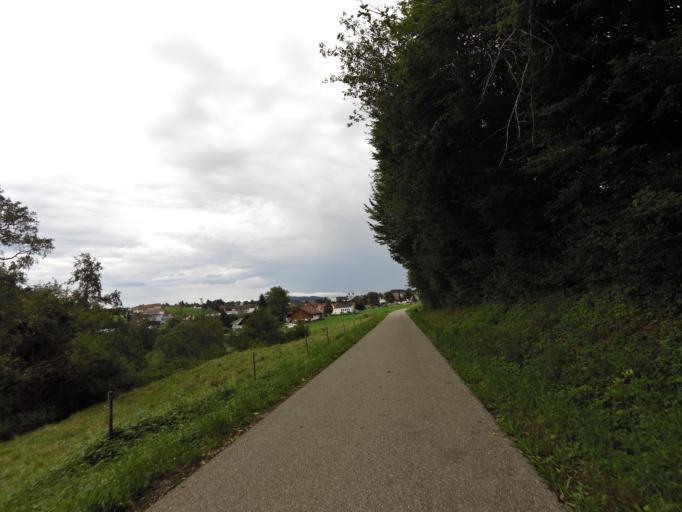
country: DE
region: Bavaria
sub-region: Swabia
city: Heimenkirch
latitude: 47.6086
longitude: 9.9042
